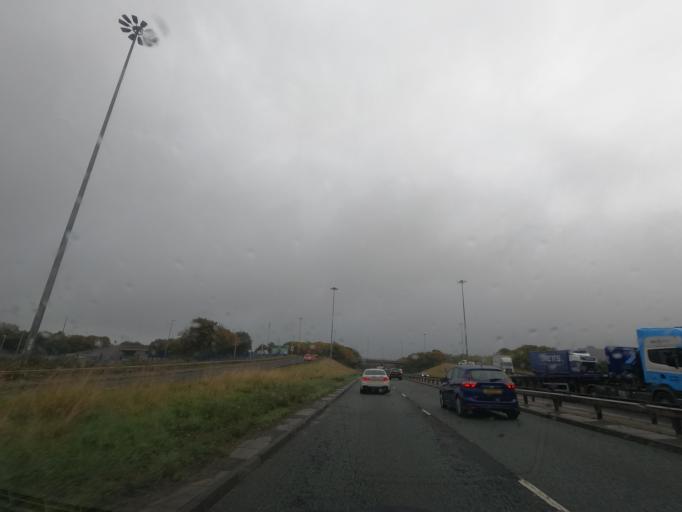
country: GB
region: England
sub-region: Middlesbrough
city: Middlesbrough
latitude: 54.5769
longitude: -1.2489
